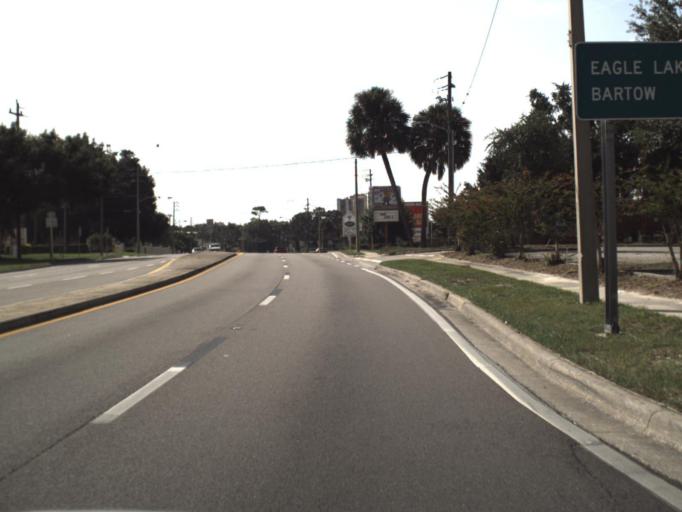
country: US
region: Florida
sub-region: Polk County
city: Winter Haven
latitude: 28.0423
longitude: -81.7349
